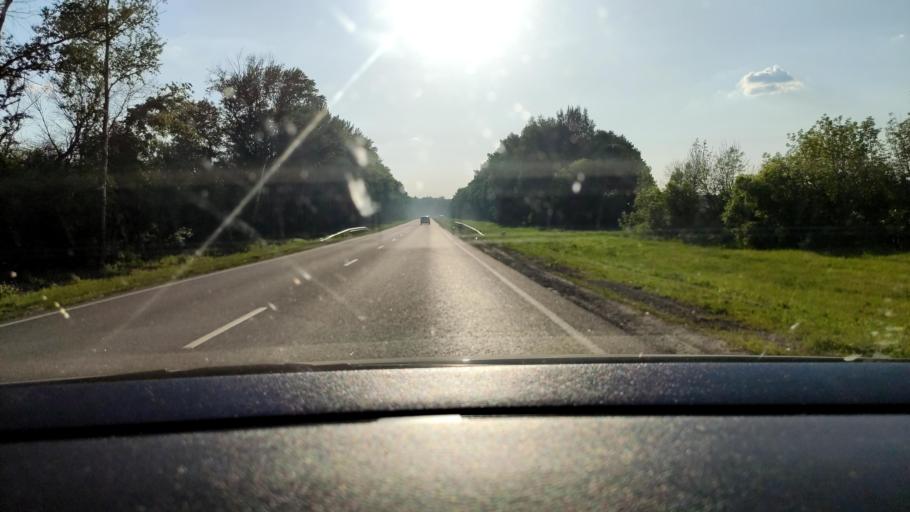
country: RU
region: Voronezj
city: Kashirskoye
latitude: 51.4640
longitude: 39.7175
